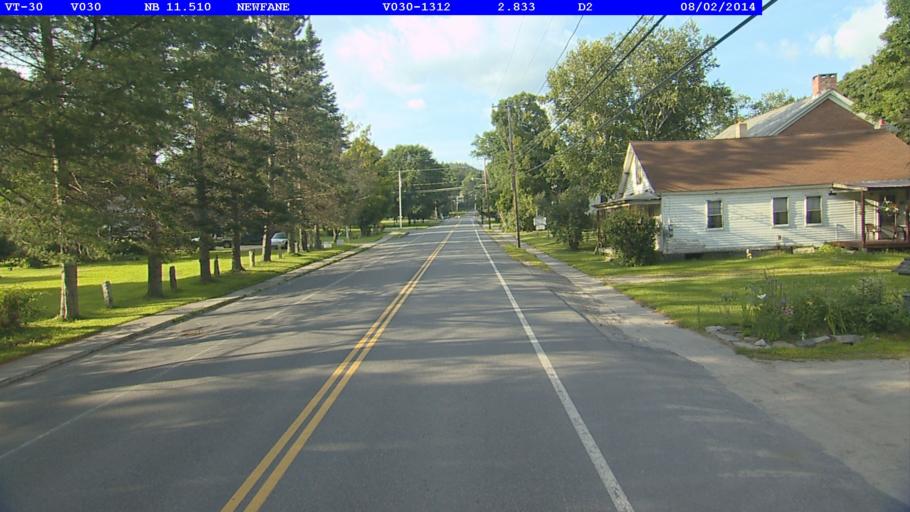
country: US
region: Vermont
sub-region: Windham County
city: Newfane
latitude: 42.9846
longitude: -72.6556
